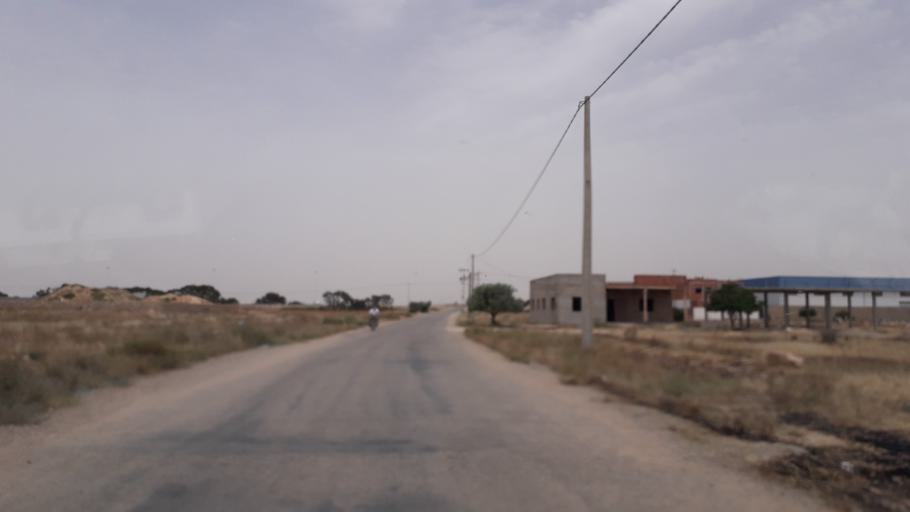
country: TN
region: Safaqis
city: Al Qarmadah
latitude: 34.8483
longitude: 10.7538
